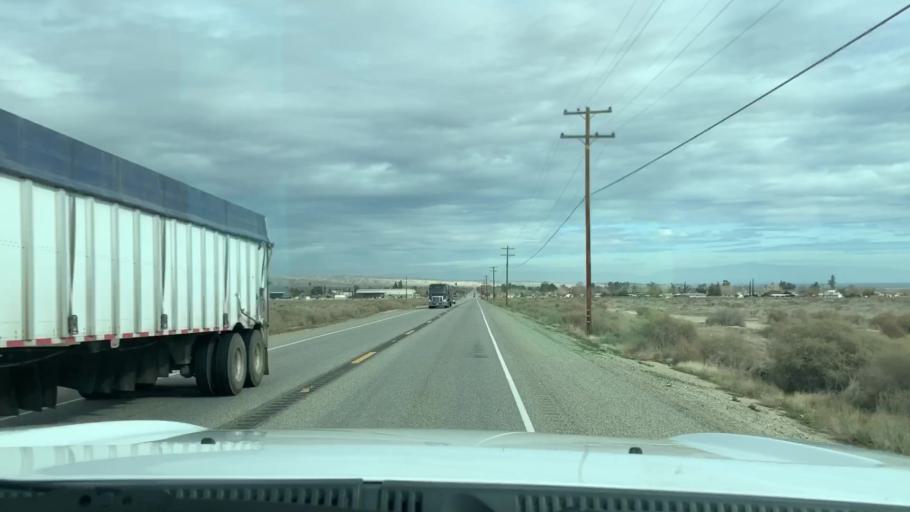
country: US
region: California
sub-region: Kern County
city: Ford City
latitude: 35.2013
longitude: -119.4175
